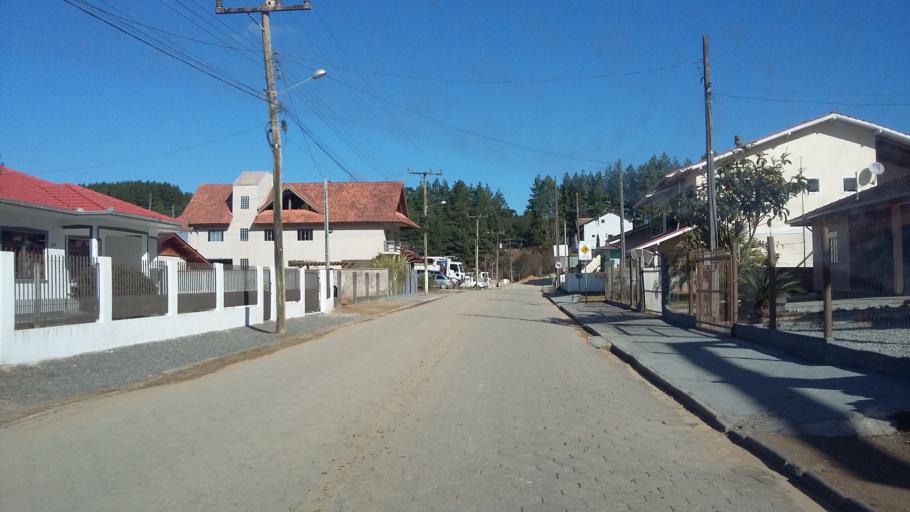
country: BR
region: Santa Catarina
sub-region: Santo Amaro Da Imperatriz
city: Santo Amaro da Imperatriz
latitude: -27.6754
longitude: -49.0123
